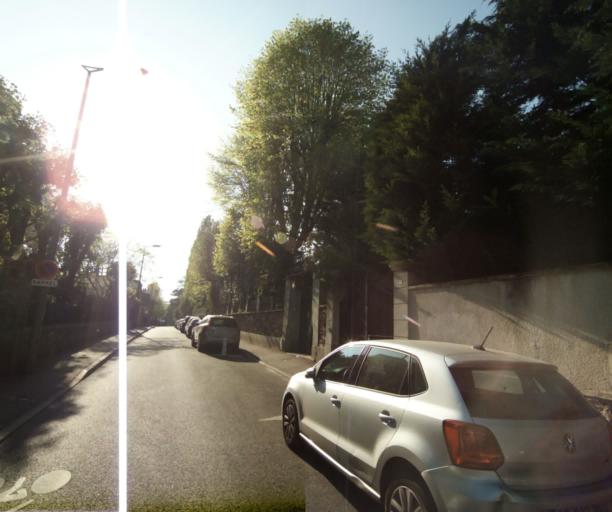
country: FR
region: Ile-de-France
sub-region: Departement des Hauts-de-Seine
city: Ville-d'Avray
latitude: 48.8278
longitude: 2.2046
